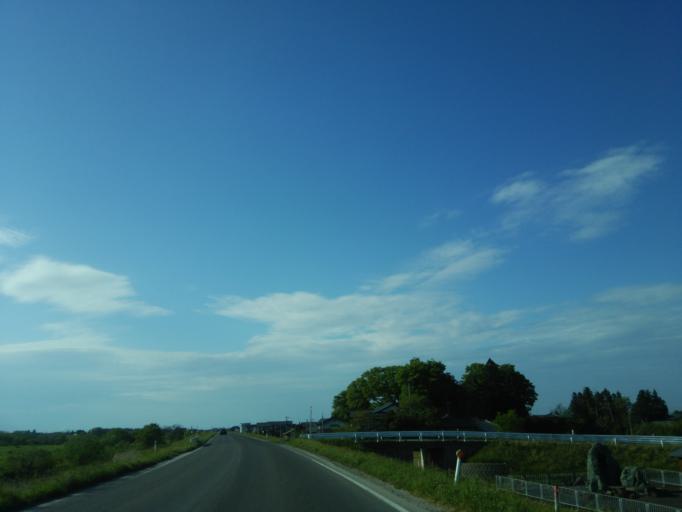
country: JP
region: Niigata
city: Niitsu-honcho
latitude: 37.7994
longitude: 139.1841
